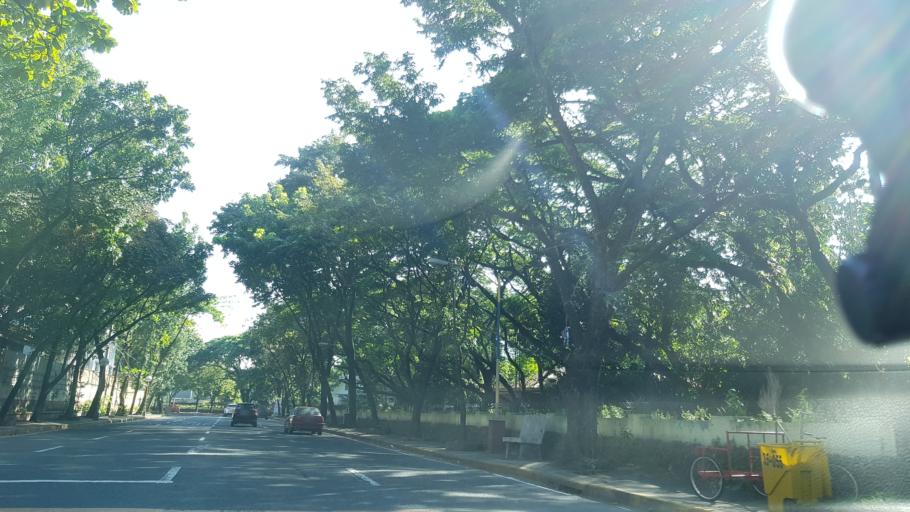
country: PH
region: Metro Manila
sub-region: Pasig
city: Pasig City
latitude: 14.5822
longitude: 121.0707
